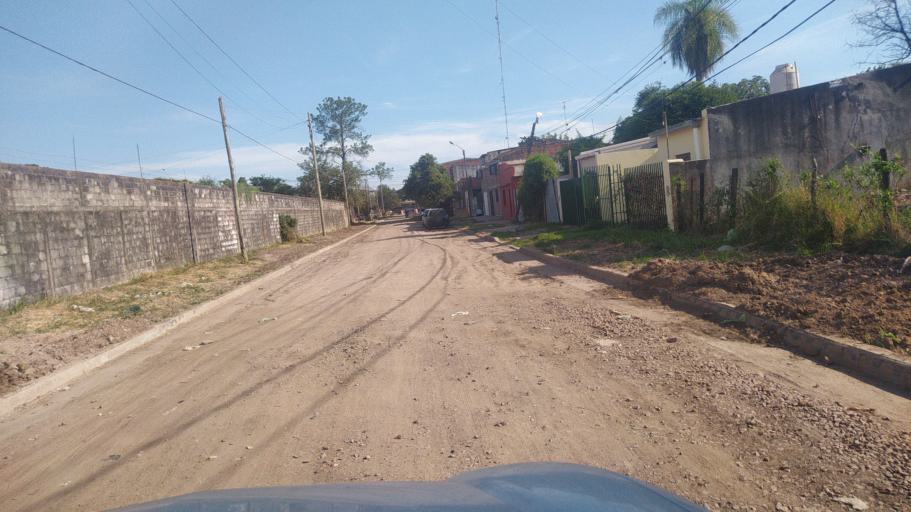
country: AR
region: Corrientes
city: Corrientes
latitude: -27.4914
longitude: -58.8156
